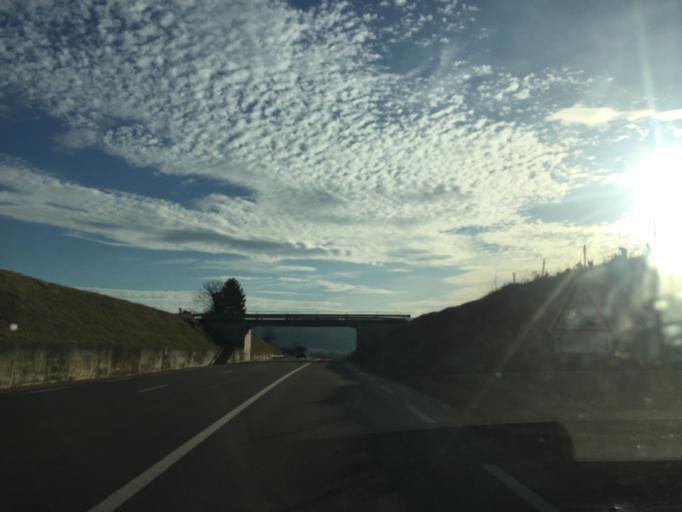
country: FR
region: Franche-Comte
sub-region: Departement du Jura
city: Arbois
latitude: 46.9305
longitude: 5.7758
